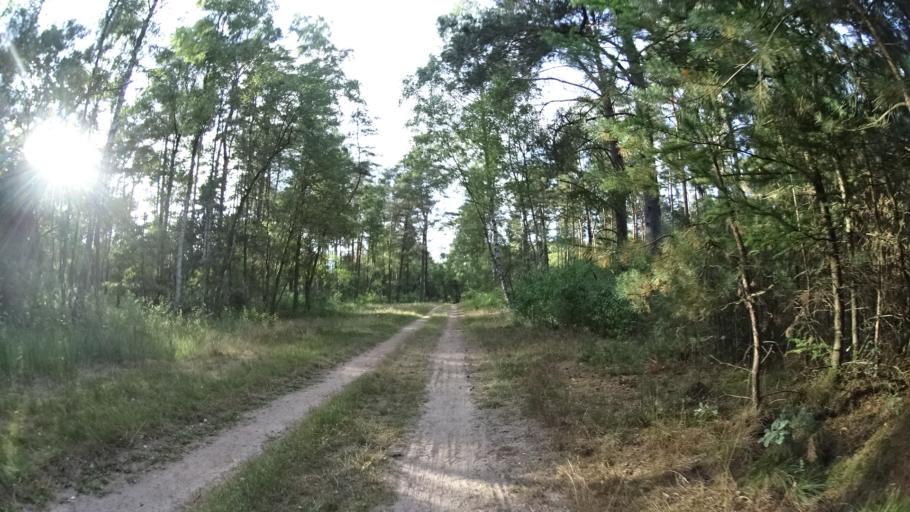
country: DE
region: Lower Saxony
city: Handeloh
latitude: 53.2206
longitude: 9.8784
